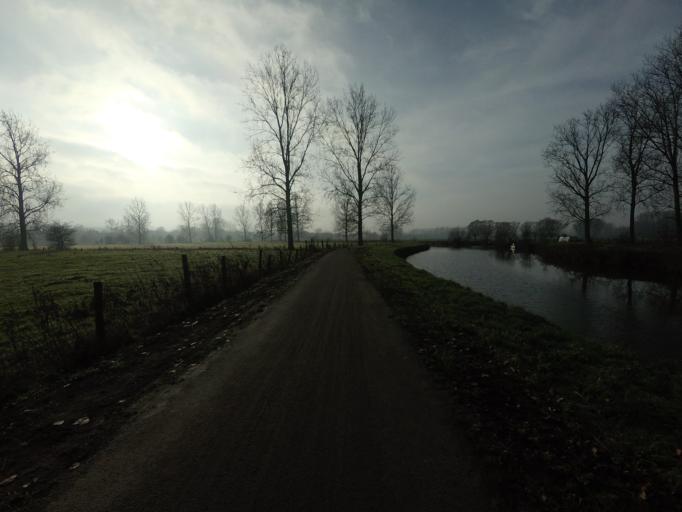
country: BE
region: Flanders
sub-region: Provincie Vlaams-Brabant
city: Galmaarden
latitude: 50.8004
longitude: 3.9559
